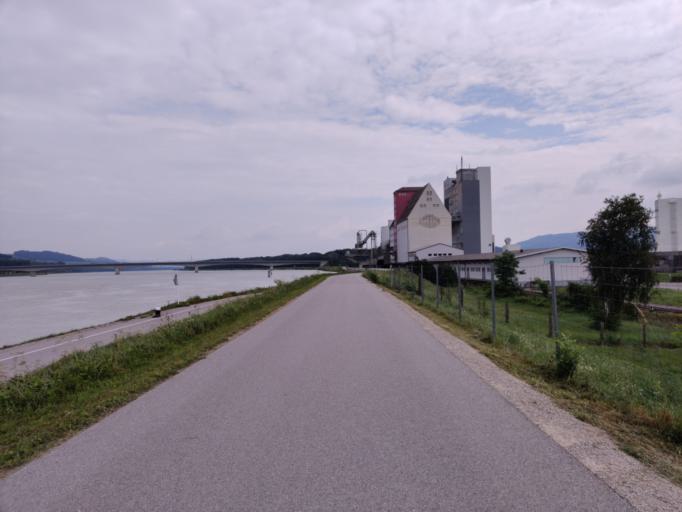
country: AT
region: Lower Austria
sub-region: Politischer Bezirk Melk
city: Klein-Poechlarn
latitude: 48.2132
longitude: 15.2204
